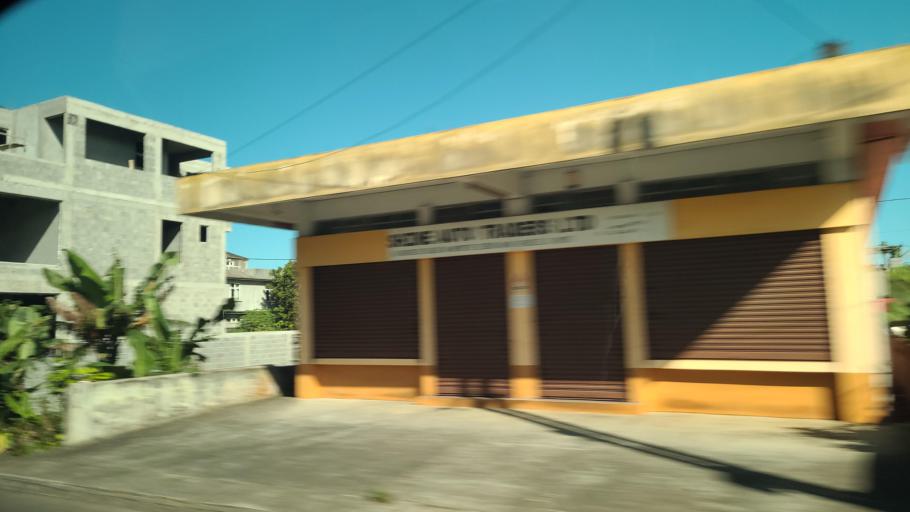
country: MU
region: Flacq
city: Lalmatie
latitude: -20.2053
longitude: 57.6758
